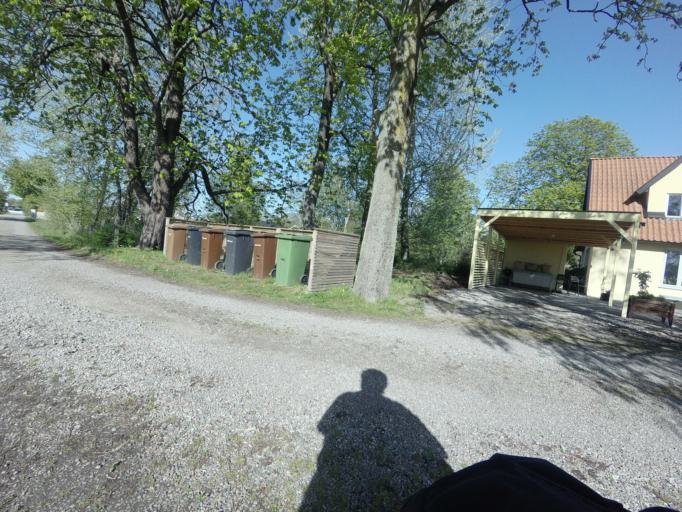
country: SE
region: Skane
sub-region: Landskrona
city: Asmundtorp
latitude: 55.8549
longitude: 12.9042
